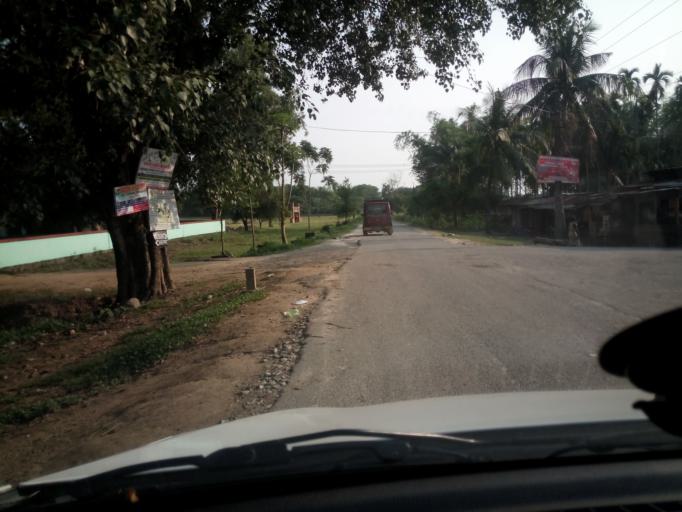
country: IN
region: Assam
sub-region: Udalguri
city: Udalguri
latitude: 26.7159
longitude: 92.0741
